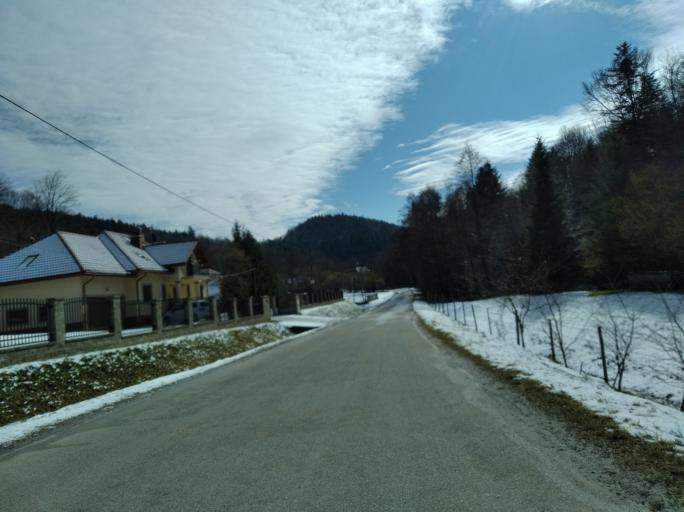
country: PL
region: Subcarpathian Voivodeship
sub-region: Powiat brzozowski
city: Jablonica Polska
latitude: 49.7453
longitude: 21.8830
